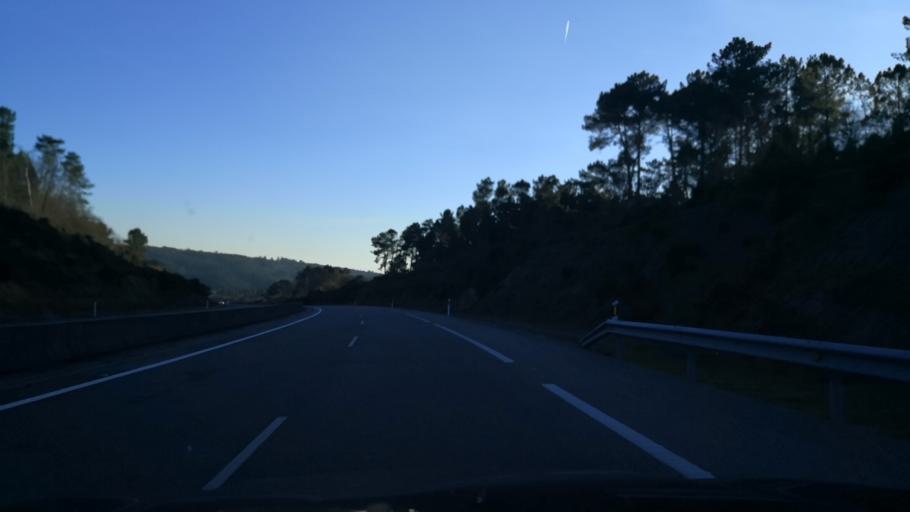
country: ES
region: Galicia
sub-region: Provincia de Ourense
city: Pinor
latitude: 42.4764
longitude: -8.0266
